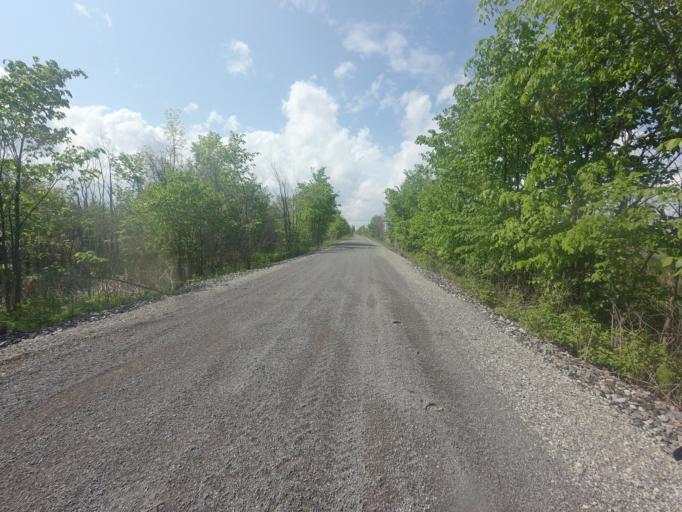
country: CA
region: Ontario
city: Carleton Place
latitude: 45.0757
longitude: -76.1020
